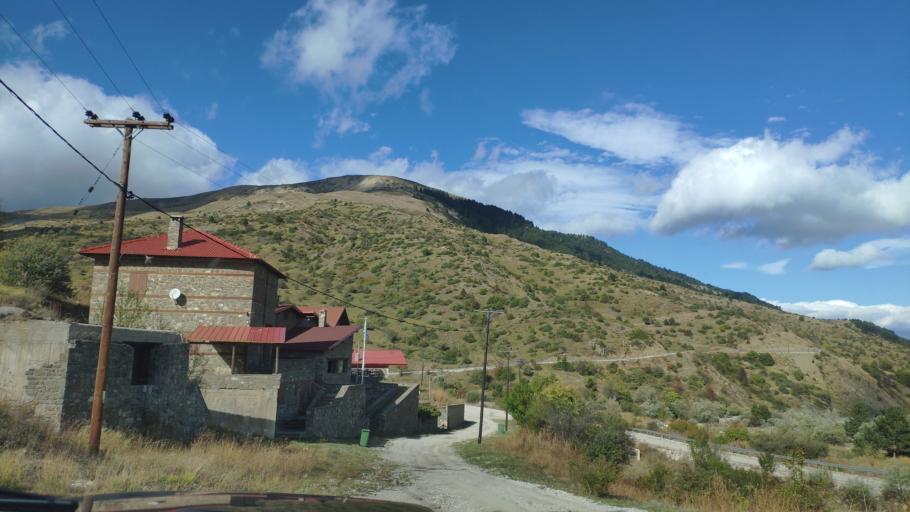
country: AL
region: Korce
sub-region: Rrethi i Devollit
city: Miras
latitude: 40.3939
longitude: 20.8368
